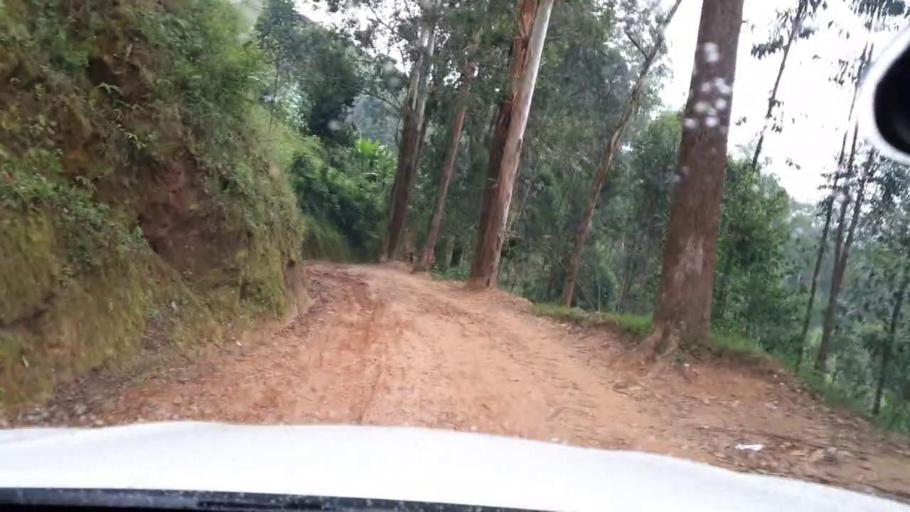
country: RW
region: Western Province
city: Cyangugu
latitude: -2.4047
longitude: 29.2106
